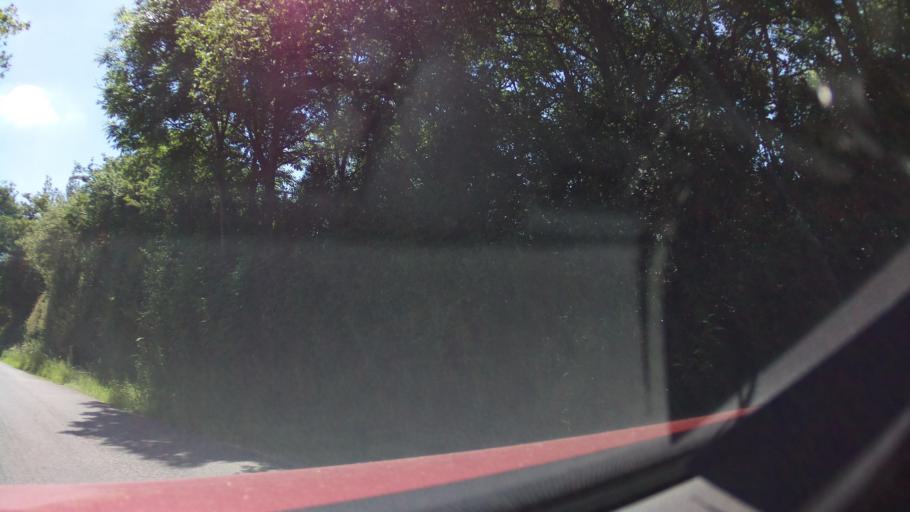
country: GB
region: England
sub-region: Wiltshire
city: Bremhill
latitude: 51.4567
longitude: -2.0638
